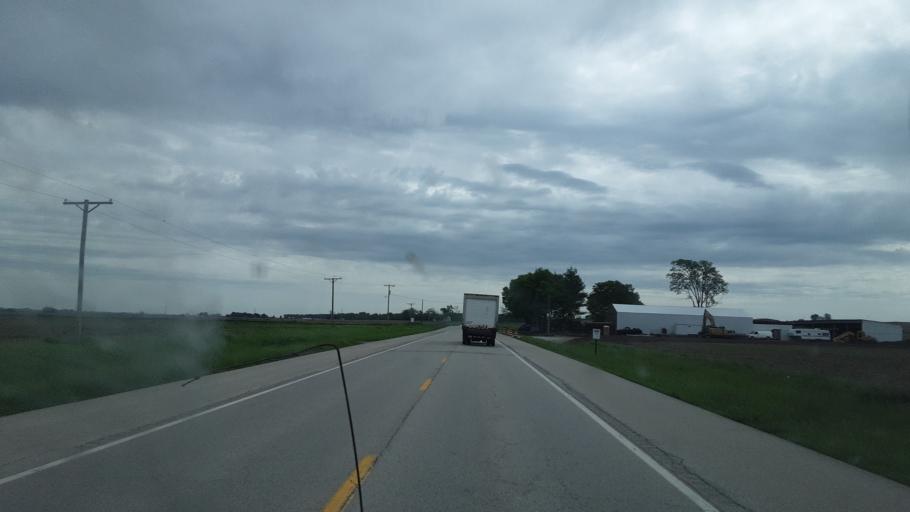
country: US
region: Illinois
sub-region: Tazewell County
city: Delavan
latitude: 40.3053
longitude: -89.6341
